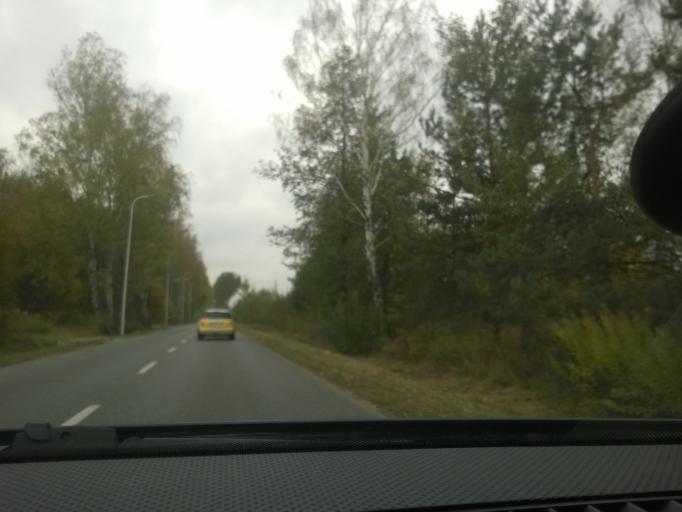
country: PL
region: Masovian Voivodeship
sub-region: Powiat pruszkowski
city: Nadarzyn
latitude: 52.1109
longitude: 20.7999
